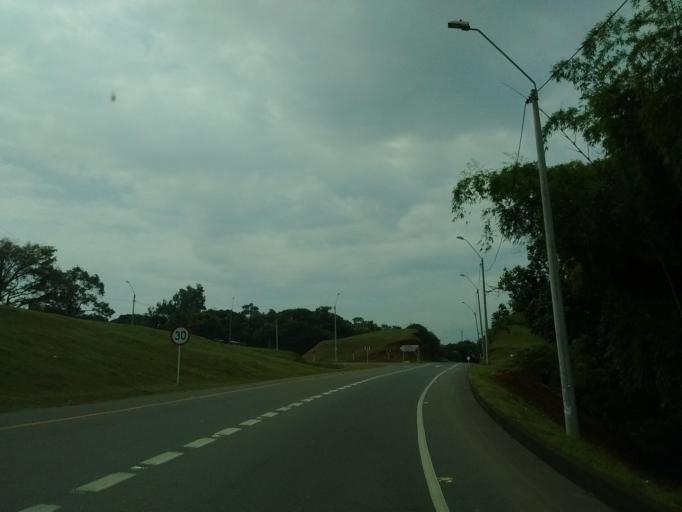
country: CO
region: Cauca
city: Santander de Quilichao
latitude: 2.9918
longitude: -76.4965
